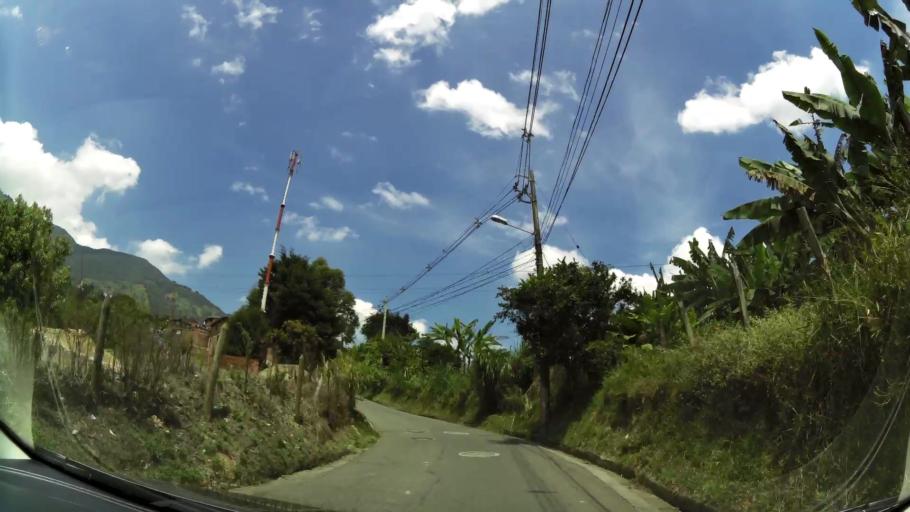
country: CO
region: Antioquia
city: La Estrella
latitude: 6.1789
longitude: -75.6539
